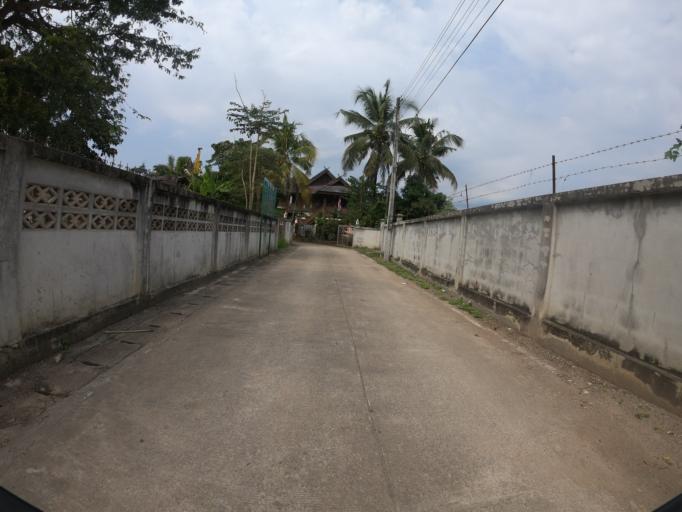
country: TH
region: Chiang Mai
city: Hang Dong
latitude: 18.7403
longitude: 98.9292
